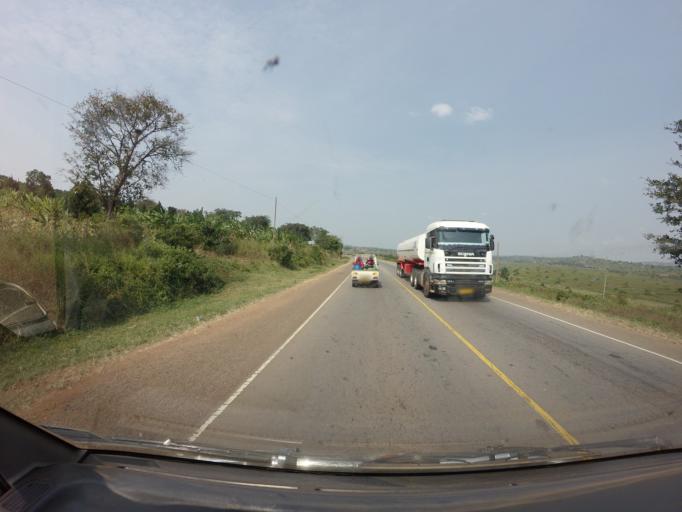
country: UG
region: Central Region
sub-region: Lwengo District
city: Lwengo
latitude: -0.4044
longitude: 31.3657
